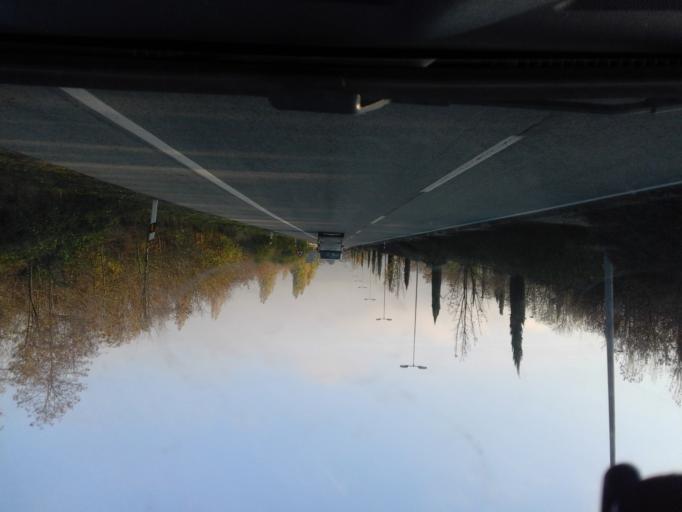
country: ES
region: Navarre
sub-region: Provincia de Navarra
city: Berriozar
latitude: 42.8314
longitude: -1.6716
